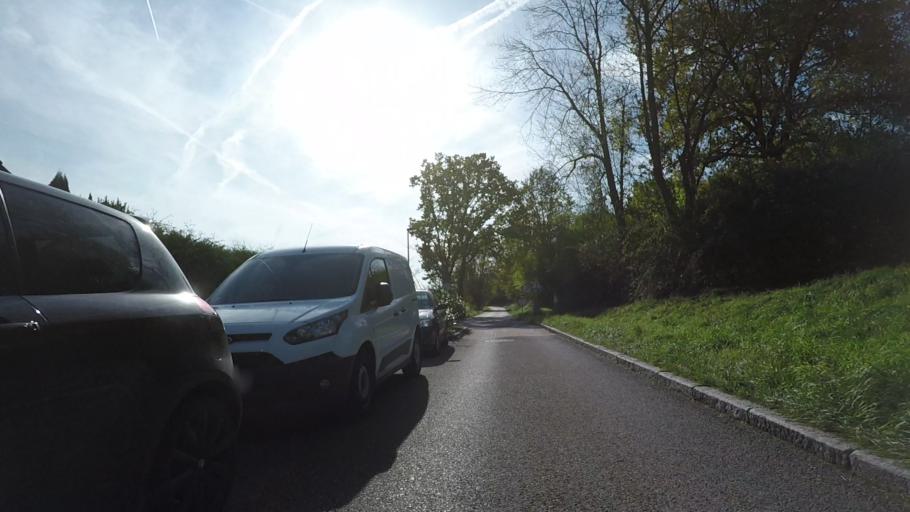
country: DE
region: Baden-Wuerttemberg
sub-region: Tuebingen Region
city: Wannweil
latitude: 48.5068
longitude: 9.1517
